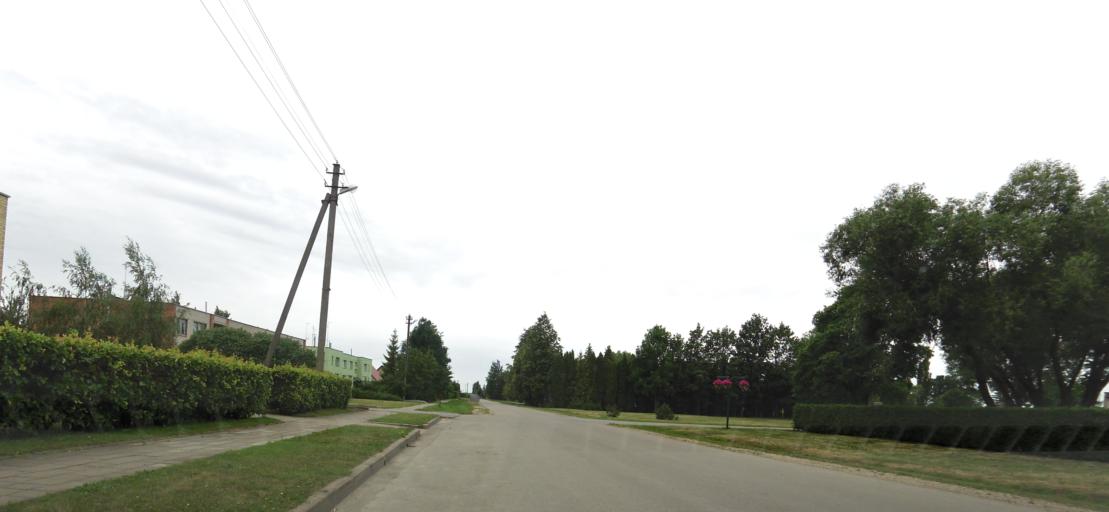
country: LT
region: Panevezys
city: Pasvalys
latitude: 56.0832
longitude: 24.5251
